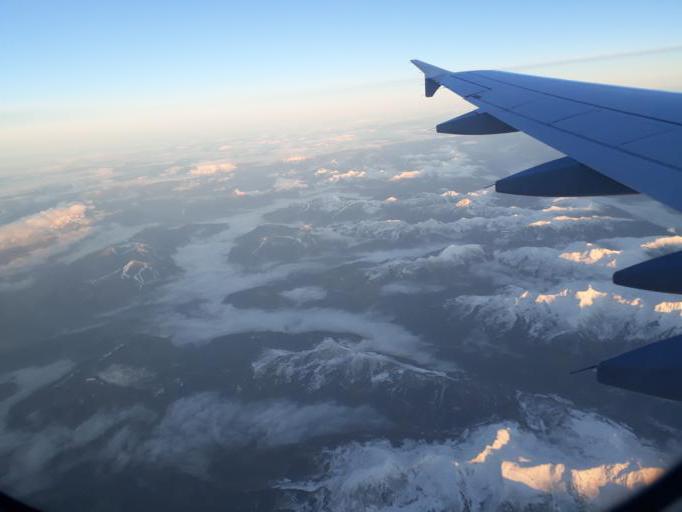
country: AT
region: Tyrol
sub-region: Politischer Bezirk Kufstein
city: Alpbach
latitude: 47.3475
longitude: 11.9228
